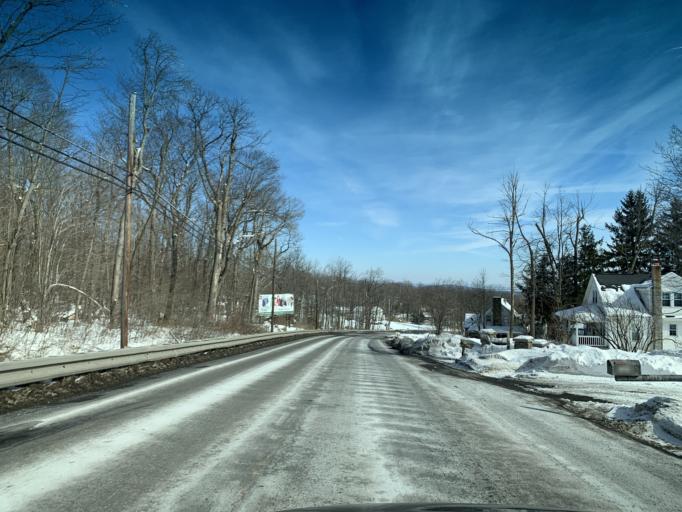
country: US
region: Maryland
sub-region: Allegany County
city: Frostburg
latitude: 39.6765
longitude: -78.9466
